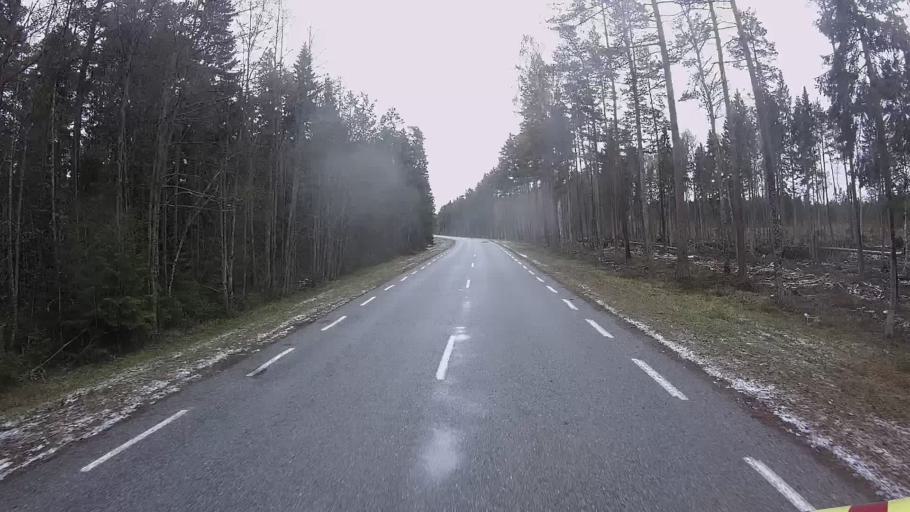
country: EE
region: Hiiumaa
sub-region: Kaerdla linn
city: Kardla
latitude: 59.0482
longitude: 22.6815
